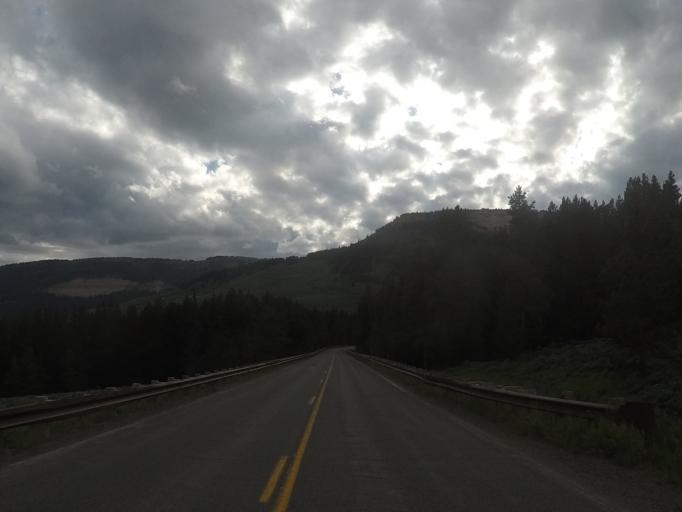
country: US
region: Wyoming
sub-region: Big Horn County
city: Greybull
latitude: 44.6171
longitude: -107.5136
